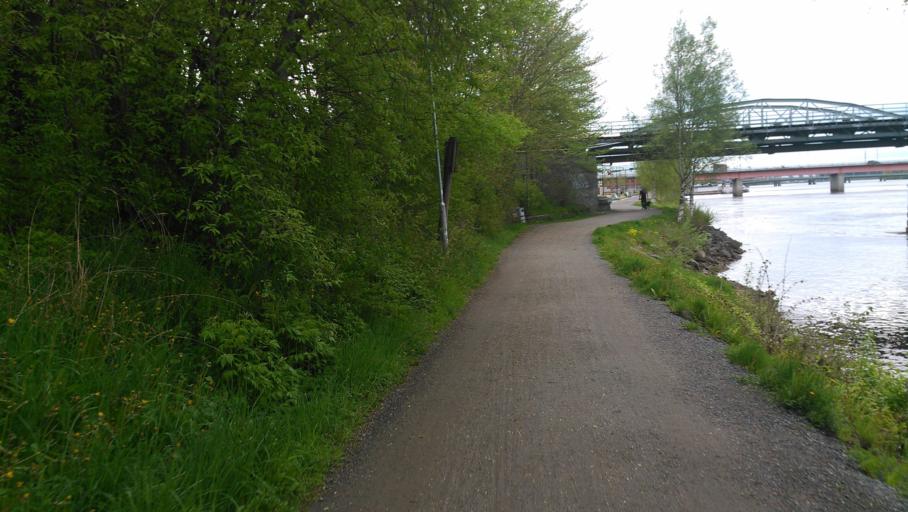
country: SE
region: Vaesterbotten
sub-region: Umea Kommun
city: Umea
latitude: 63.8264
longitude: 20.2487
